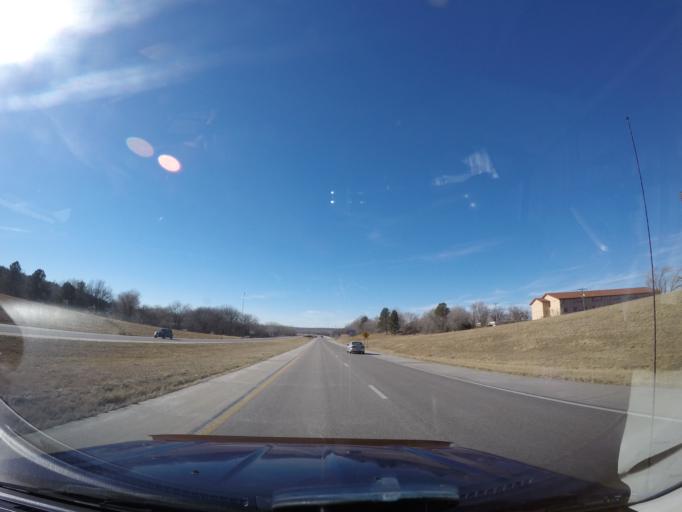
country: US
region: Kansas
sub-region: Geary County
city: Grandview Plaza
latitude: 39.0269
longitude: -96.8002
